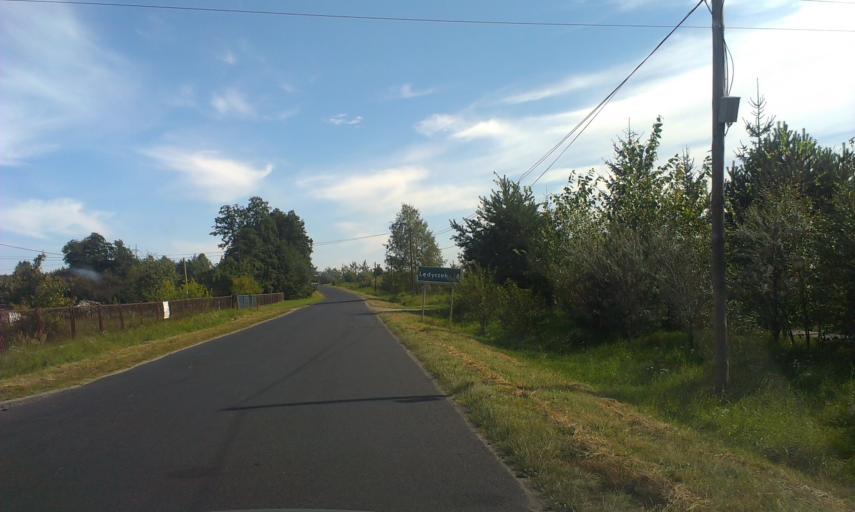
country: PL
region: Greater Poland Voivodeship
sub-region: Powiat zlotowski
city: Okonek
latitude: 53.5357
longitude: 16.8635
